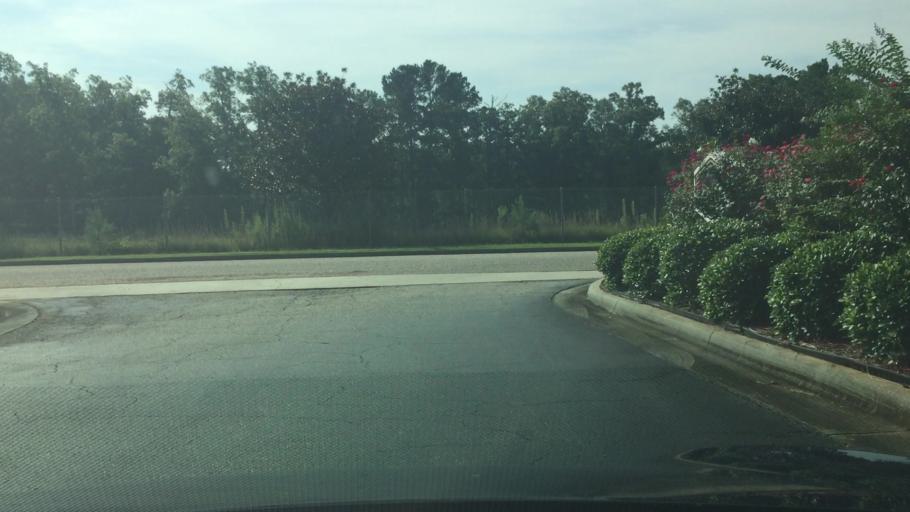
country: US
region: Alabama
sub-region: Butler County
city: Greenville
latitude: 31.8556
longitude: -86.6354
